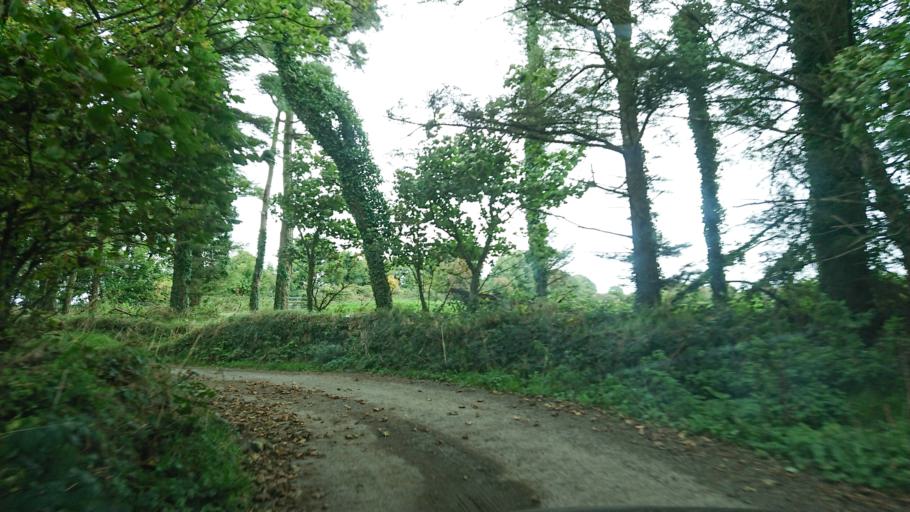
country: IE
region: Munster
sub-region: Waterford
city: Dunmore East
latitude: 52.1993
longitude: -7.0467
